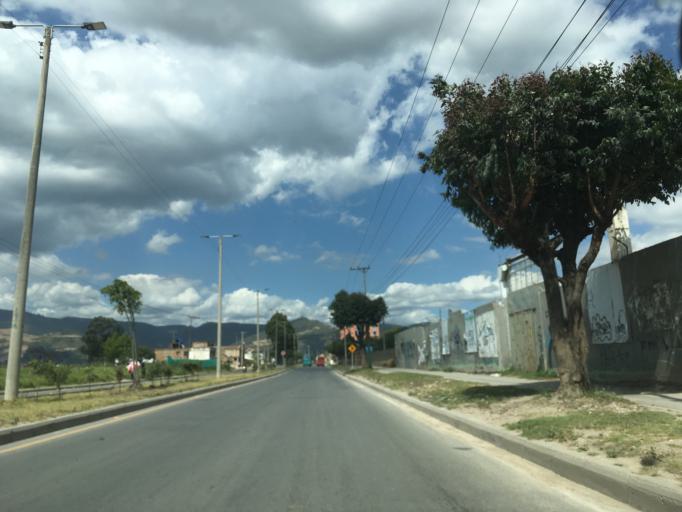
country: CO
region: Boyaca
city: Sogamoso
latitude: 5.7318
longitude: -72.9195
